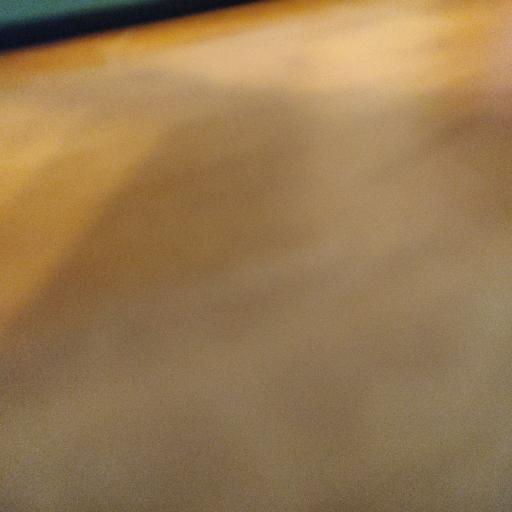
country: SE
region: Vaestmanland
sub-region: Vasteras
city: Tillberga
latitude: 59.6973
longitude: 16.6714
